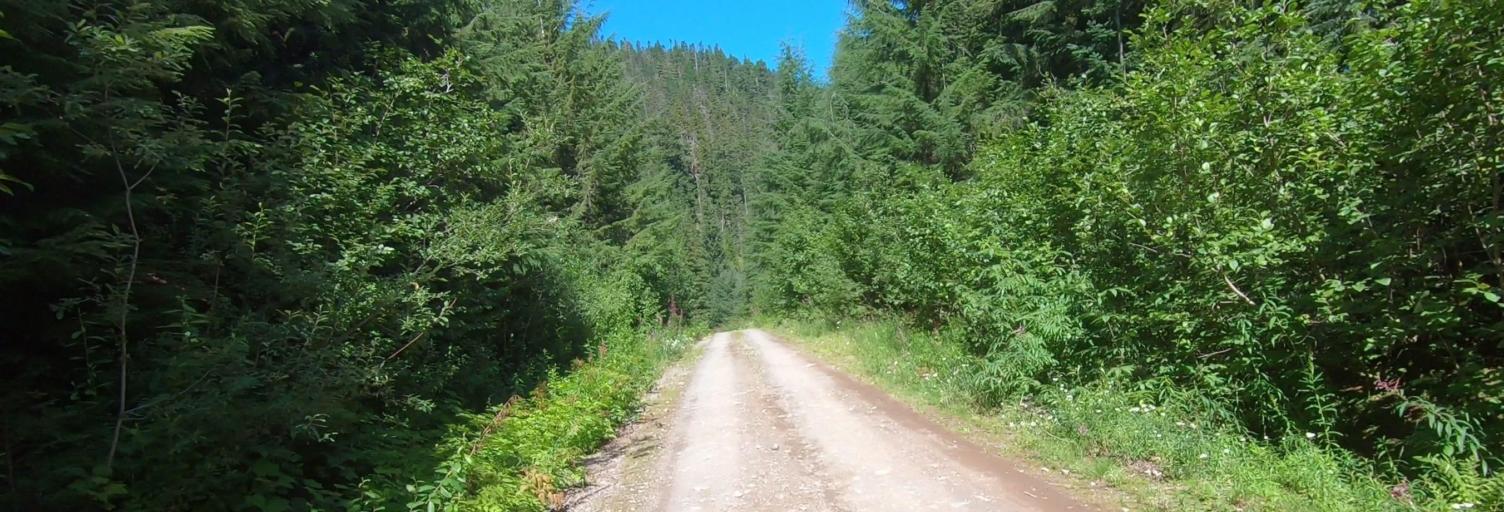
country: CA
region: British Columbia
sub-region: Fraser Valley Regional District
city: Chilliwack
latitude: 48.8537
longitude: -121.7948
